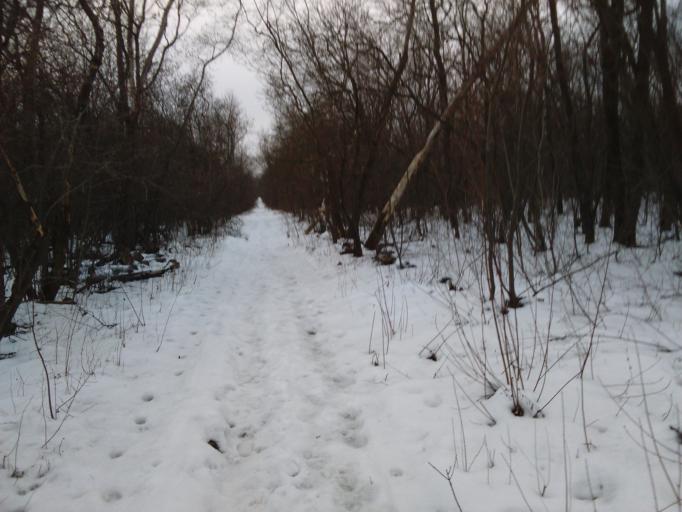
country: RU
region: Rostov
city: Temernik
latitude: 47.3519
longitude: 39.7396
